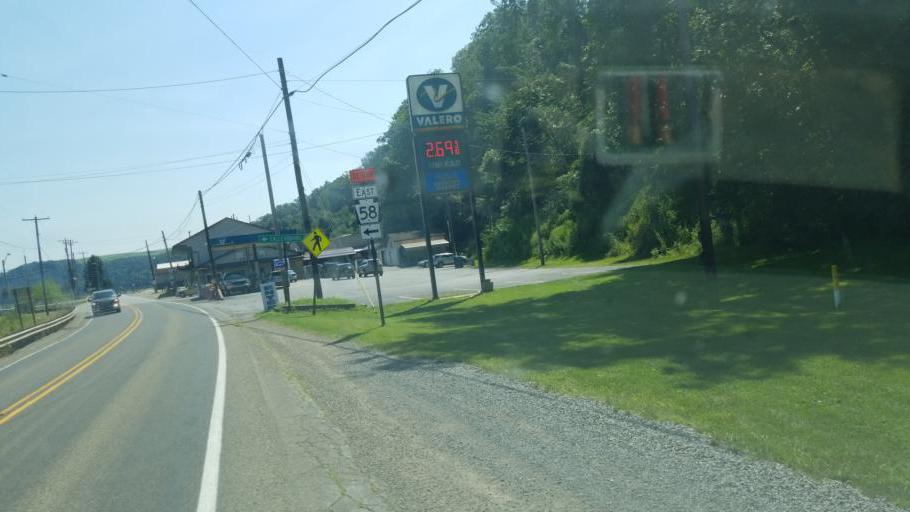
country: US
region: Pennsylvania
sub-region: Butler County
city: Chicora
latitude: 41.1036
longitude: -79.6820
